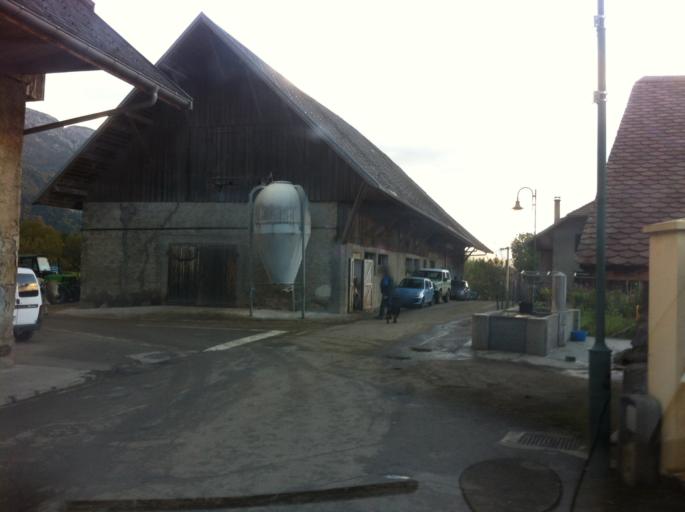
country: FR
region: Rhone-Alpes
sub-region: Departement de la Haute-Savoie
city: Doussard
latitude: 45.7626
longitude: 6.2199
